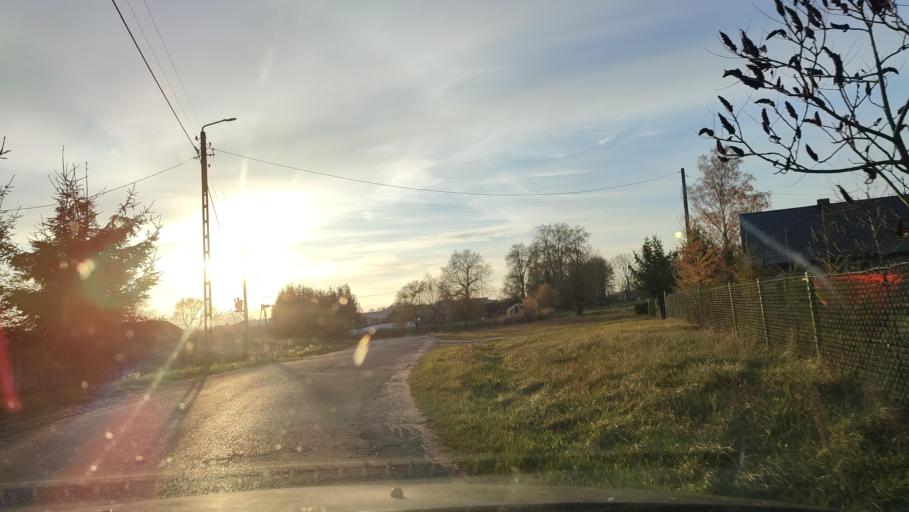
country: PL
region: Masovian Voivodeship
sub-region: Powiat mlawski
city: Dzierzgowo
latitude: 53.2630
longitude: 20.6236
